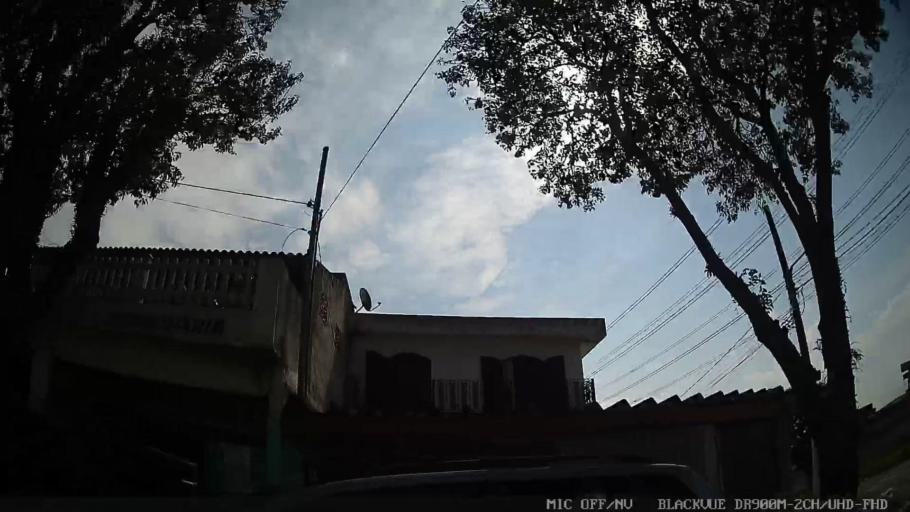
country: BR
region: Sao Paulo
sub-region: Ferraz De Vasconcelos
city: Ferraz de Vasconcelos
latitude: -23.5140
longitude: -46.4149
